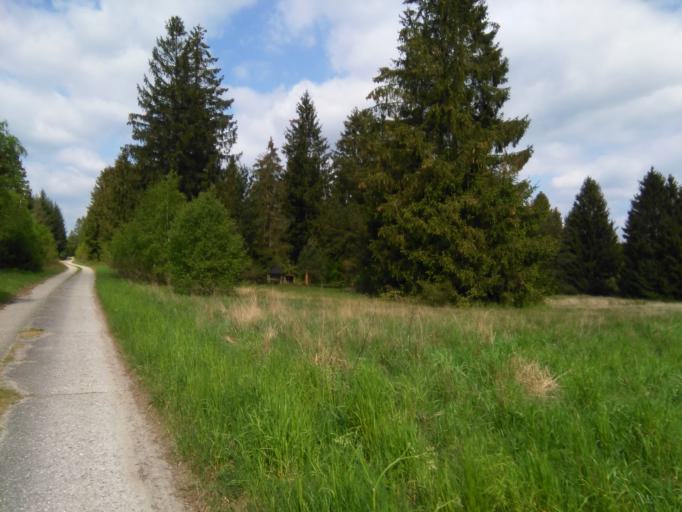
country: DK
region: Central Jutland
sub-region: Silkeborg Kommune
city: Svejbaek
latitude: 56.0546
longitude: 9.6634
